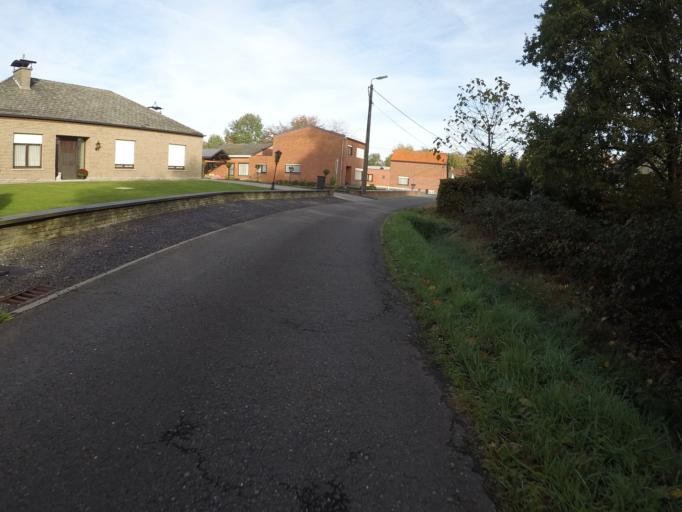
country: BE
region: Flanders
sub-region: Provincie Vlaams-Brabant
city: Begijnendijk
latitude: 51.0028
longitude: 4.7723
